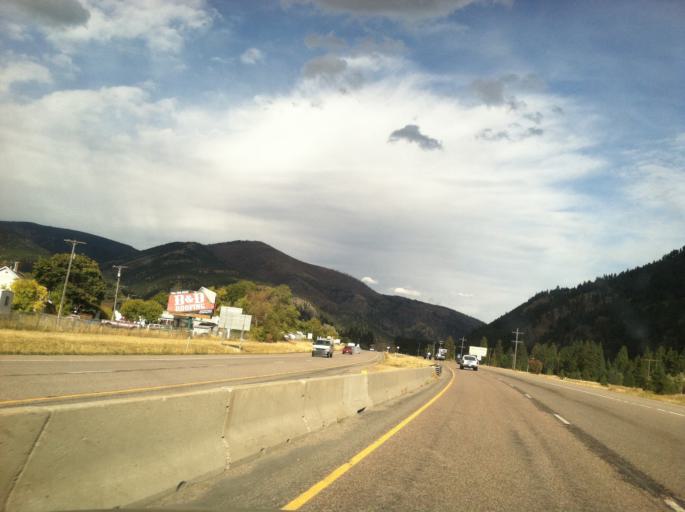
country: US
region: Montana
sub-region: Missoula County
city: East Missoula
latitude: 46.8678
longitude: -113.9463
